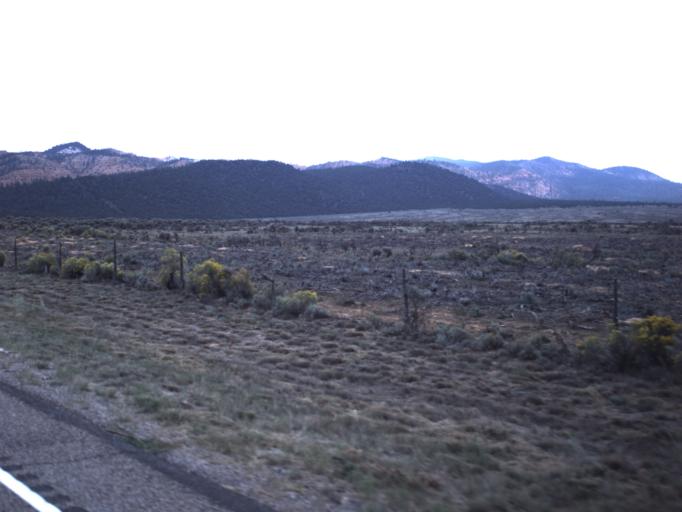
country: US
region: Utah
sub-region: Garfield County
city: Panguitch
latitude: 37.7468
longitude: -112.3514
